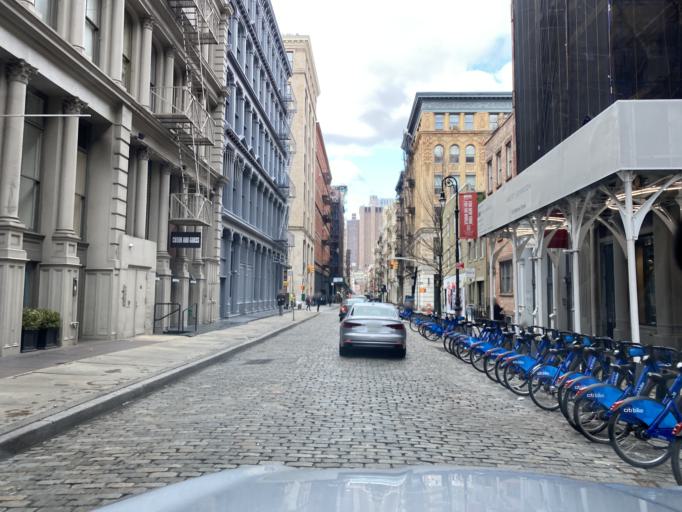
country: US
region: New York
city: New York City
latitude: 40.7235
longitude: -73.9990
